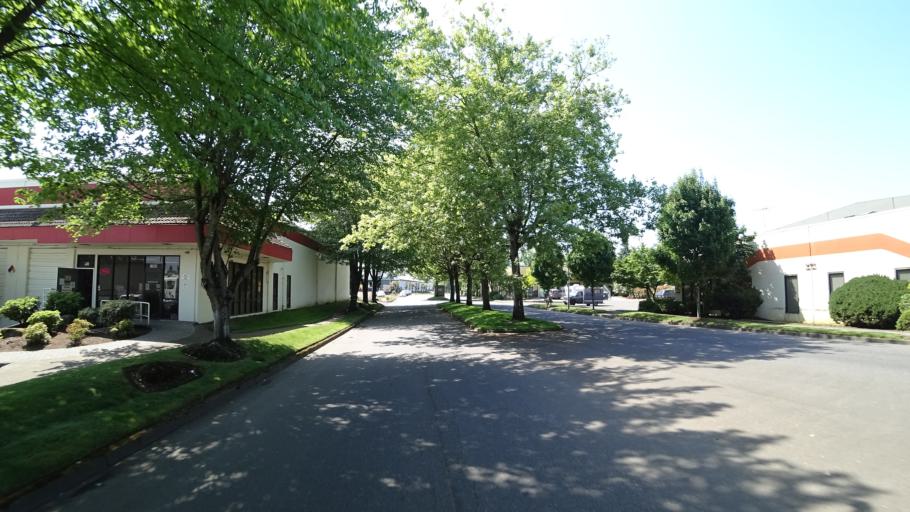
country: US
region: Oregon
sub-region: Multnomah County
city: Lents
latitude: 45.5597
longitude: -122.5426
